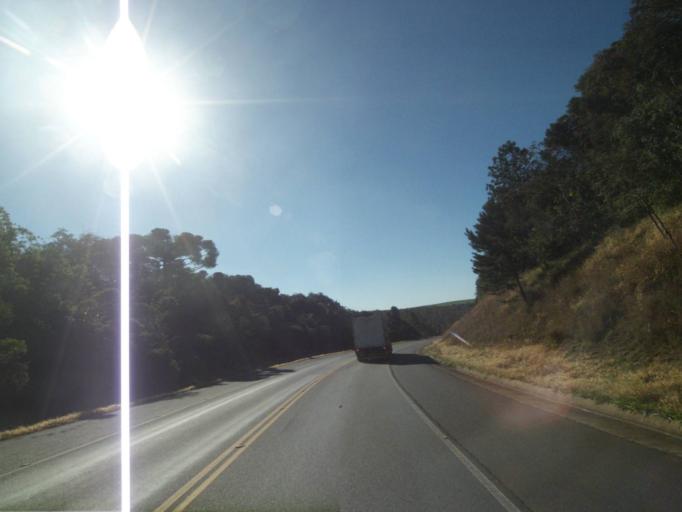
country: BR
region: Parana
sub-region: Tibagi
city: Tibagi
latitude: -24.5541
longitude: -50.4566
